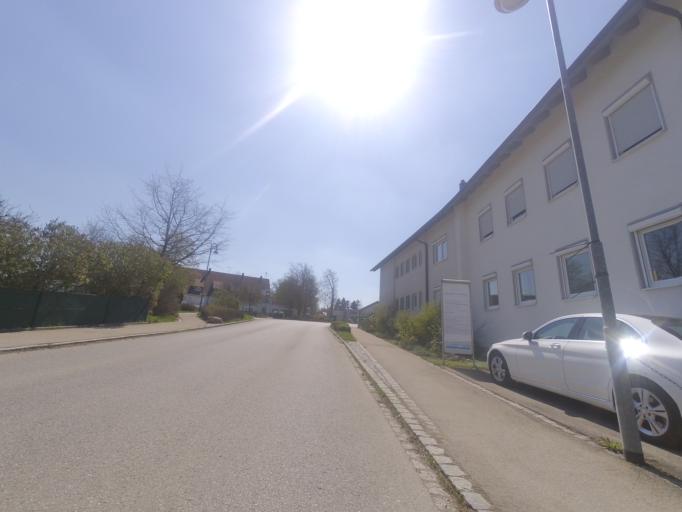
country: DE
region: Bavaria
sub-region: Swabia
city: Roggenburg
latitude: 48.2787
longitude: 10.2304
